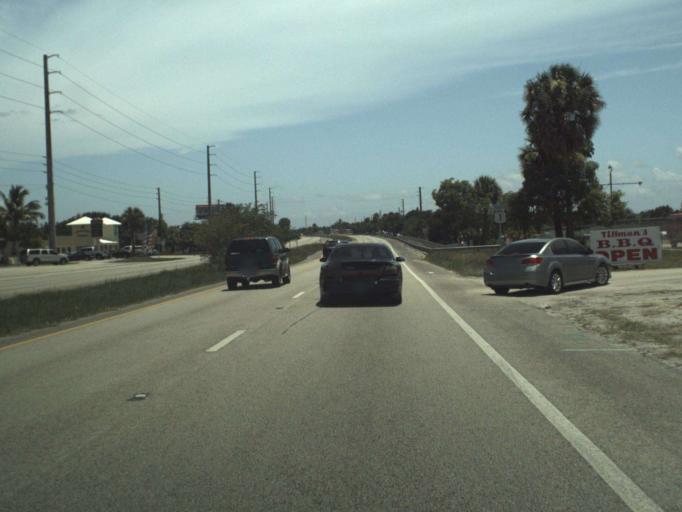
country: US
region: Florida
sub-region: Saint Lucie County
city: Fort Pierce North
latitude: 27.4840
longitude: -80.3408
